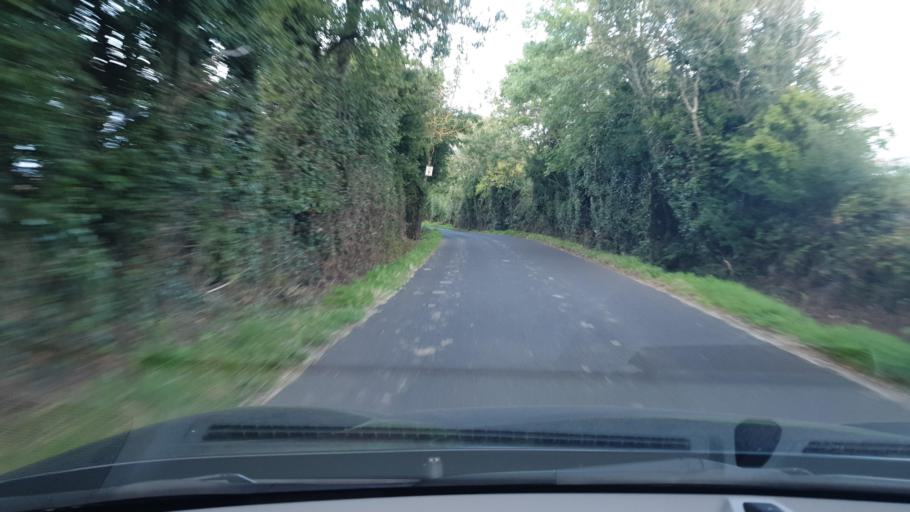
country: IE
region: Leinster
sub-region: South Dublin
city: Rathcoole
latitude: 53.2727
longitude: -6.4921
